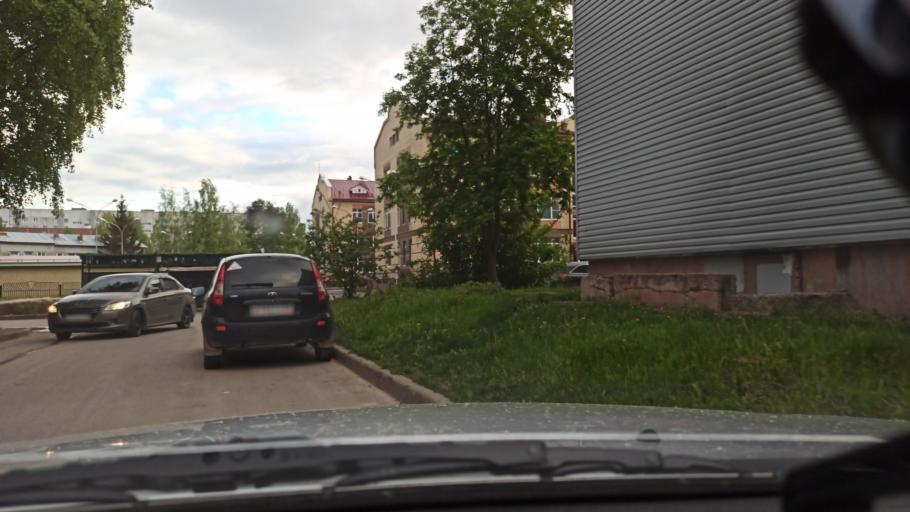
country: RU
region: Vologda
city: Vologda
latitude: 59.1957
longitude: 39.8740
